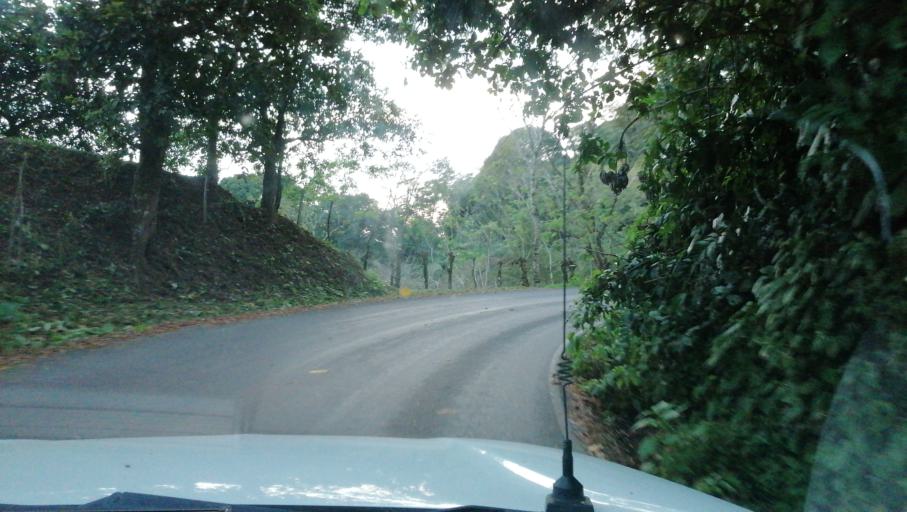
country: MX
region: Chiapas
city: Ostuacan
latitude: 17.4263
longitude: -93.3458
